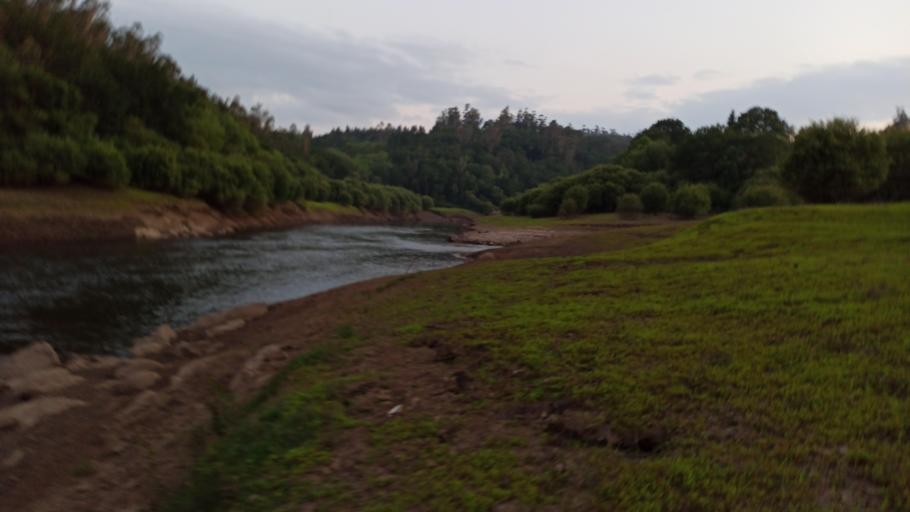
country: ES
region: Galicia
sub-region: Provincia da Coruna
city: Negreira
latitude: 42.9010
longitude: -8.7351
